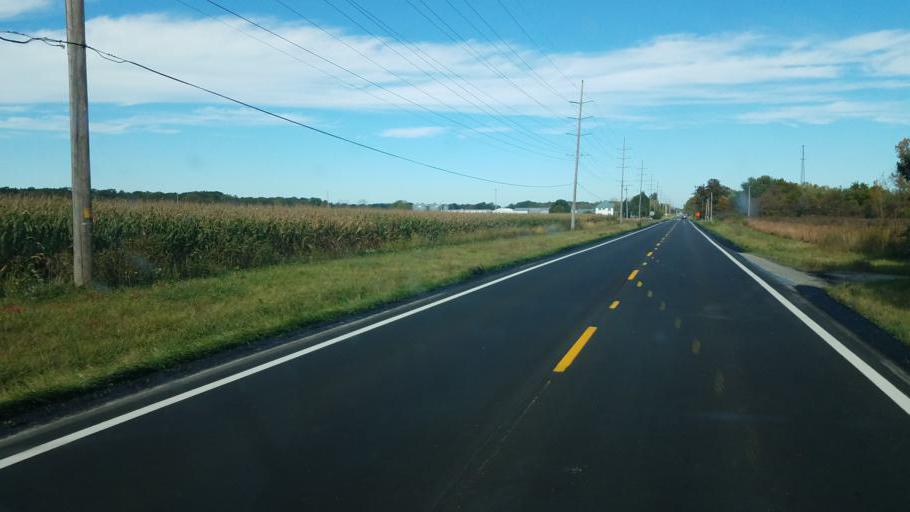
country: US
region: Ohio
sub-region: Erie County
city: Huron
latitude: 41.3443
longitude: -82.4938
